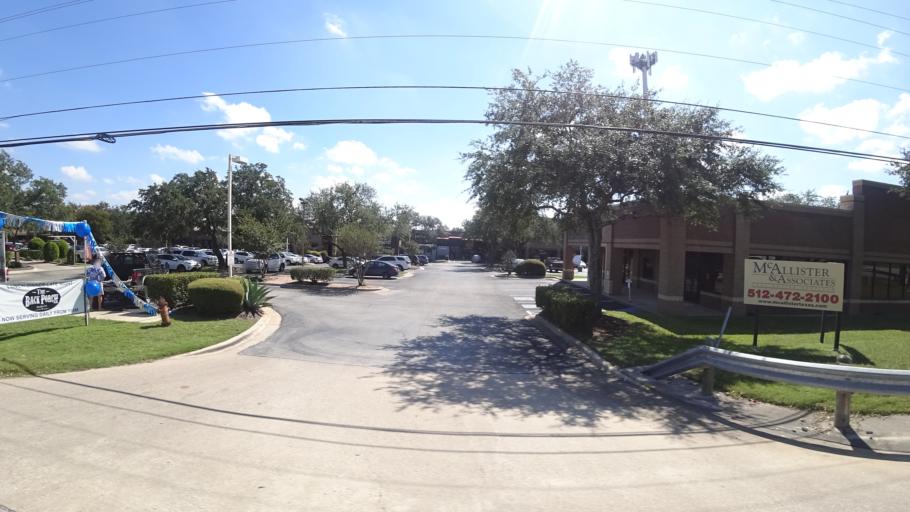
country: US
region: Texas
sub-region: Williamson County
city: Anderson Mill
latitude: 30.4623
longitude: -97.8155
